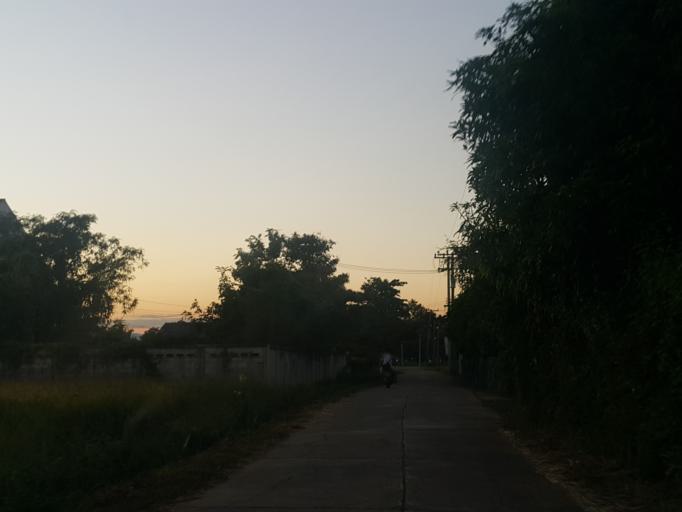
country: TH
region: Chiang Mai
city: San Kamphaeng
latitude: 18.8262
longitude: 99.1291
